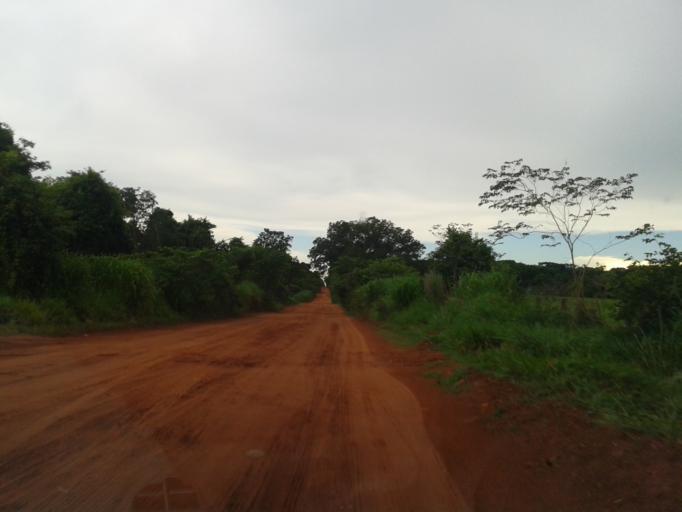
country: BR
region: Minas Gerais
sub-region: Santa Vitoria
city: Santa Vitoria
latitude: -19.1221
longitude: -50.5384
